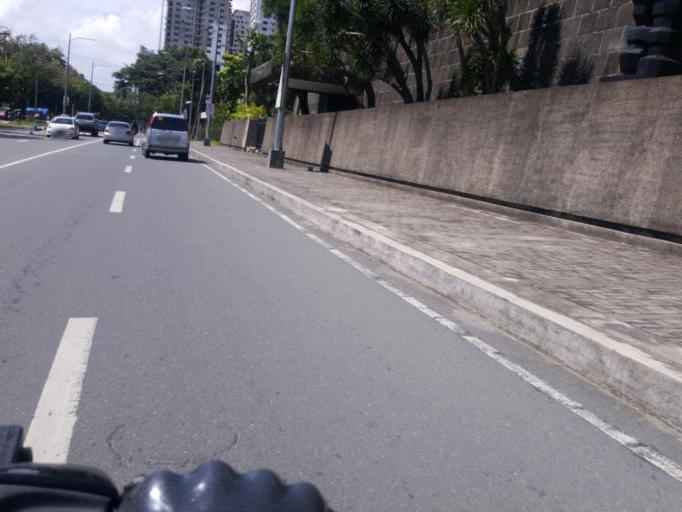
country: PH
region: Metro Manila
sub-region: City of Manila
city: Port Area
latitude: 14.5621
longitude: 120.9864
